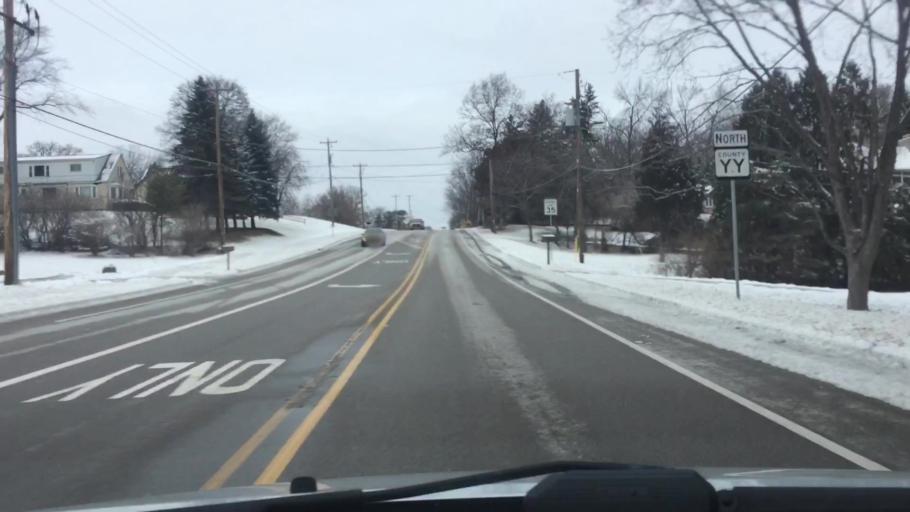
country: US
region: Wisconsin
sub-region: Waukesha County
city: Brookfield
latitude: 43.0754
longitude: -88.1059
